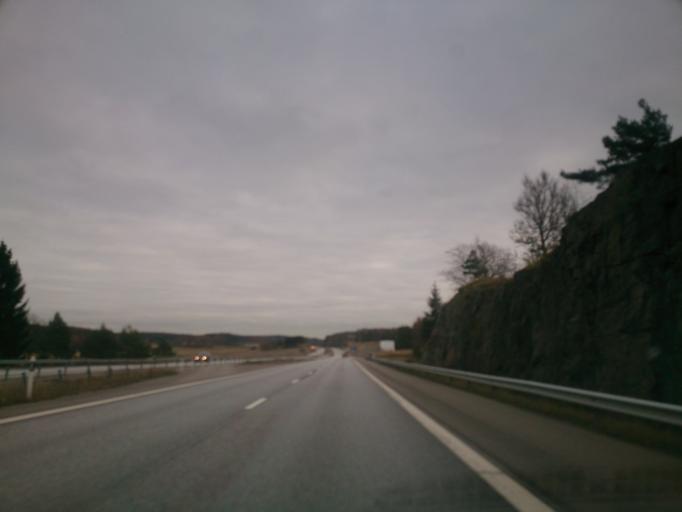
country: SE
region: Soedermanland
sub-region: Trosa Kommun
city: Vagnharad
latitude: 58.9599
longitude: 17.4675
